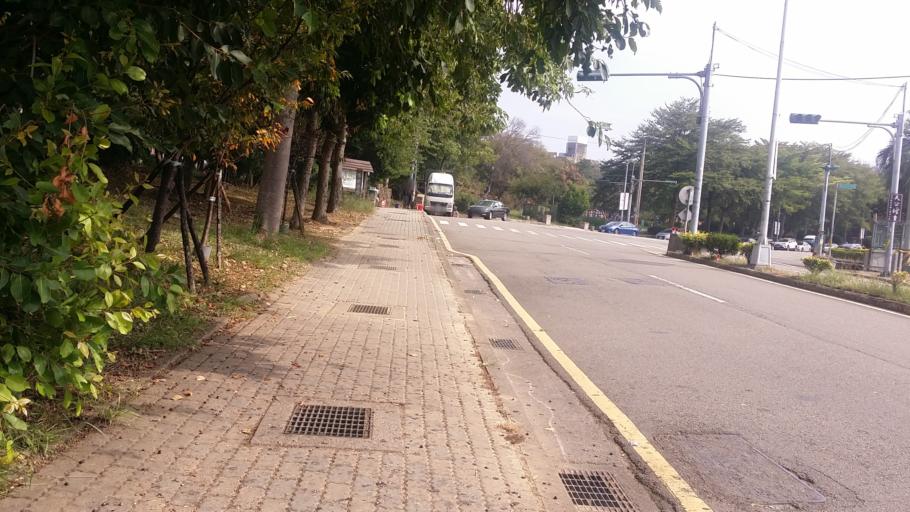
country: TW
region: Taiwan
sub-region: Hsinchu
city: Hsinchu
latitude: 24.7998
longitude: 120.9765
